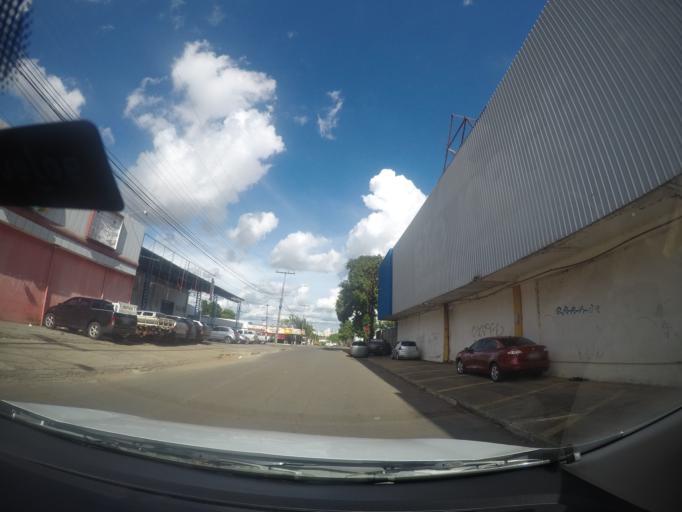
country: BR
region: Goias
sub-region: Goiania
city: Goiania
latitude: -16.6787
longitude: -49.3071
